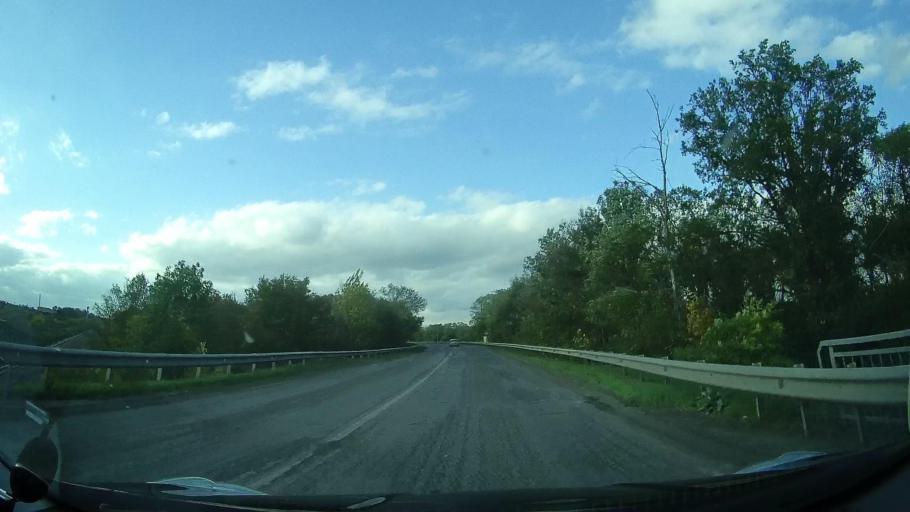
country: RU
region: Rostov
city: Kirovskaya
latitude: 46.9651
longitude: 40.0689
